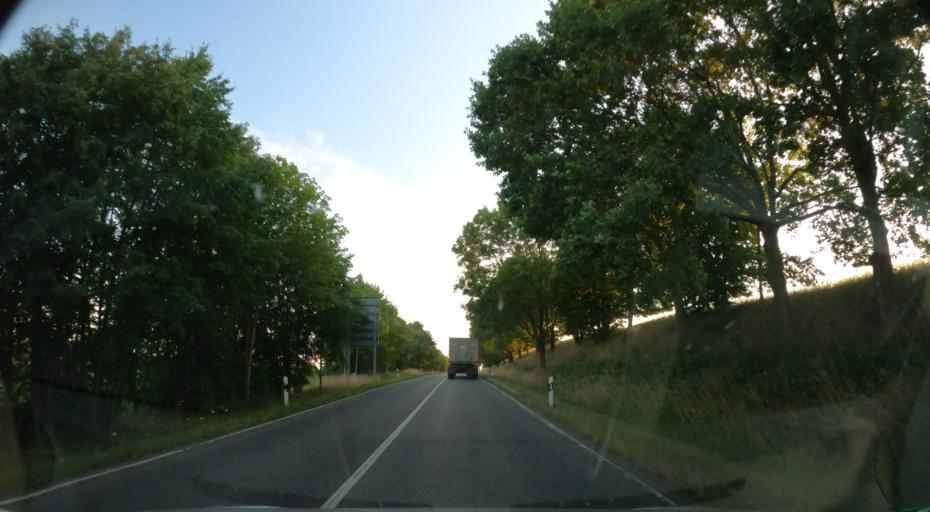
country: DE
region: Mecklenburg-Vorpommern
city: Strasburg
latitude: 53.4889
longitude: 13.6834
